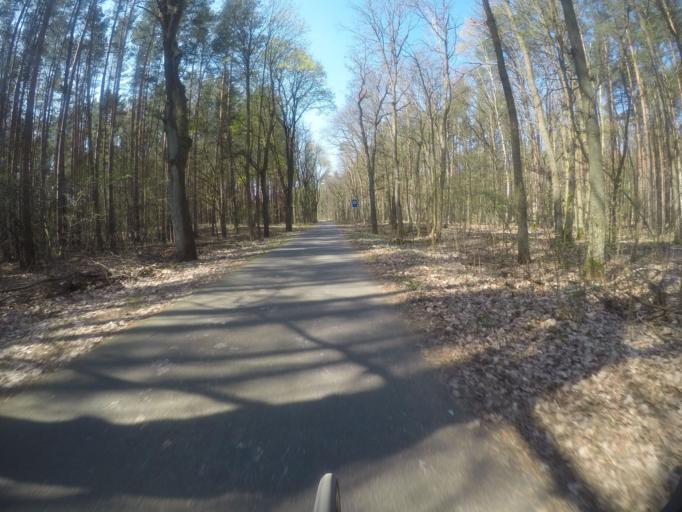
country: DE
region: Brandenburg
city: Brieselang
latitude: 52.6378
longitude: 13.0598
